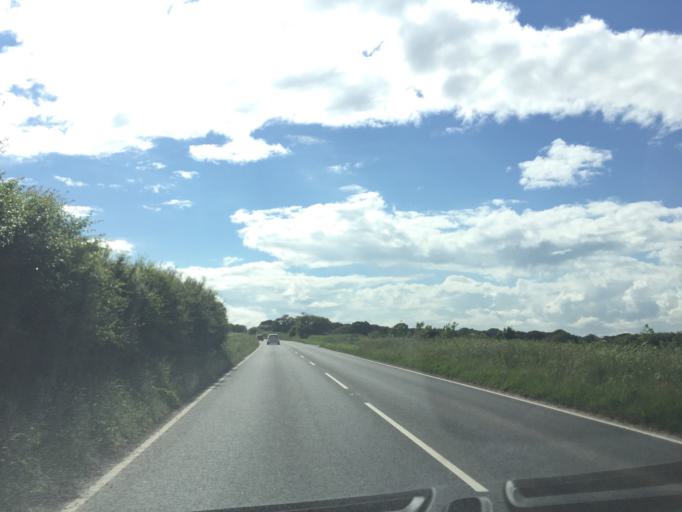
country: GB
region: England
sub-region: Dorset
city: Bovington Camp
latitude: 50.6635
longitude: -2.2921
